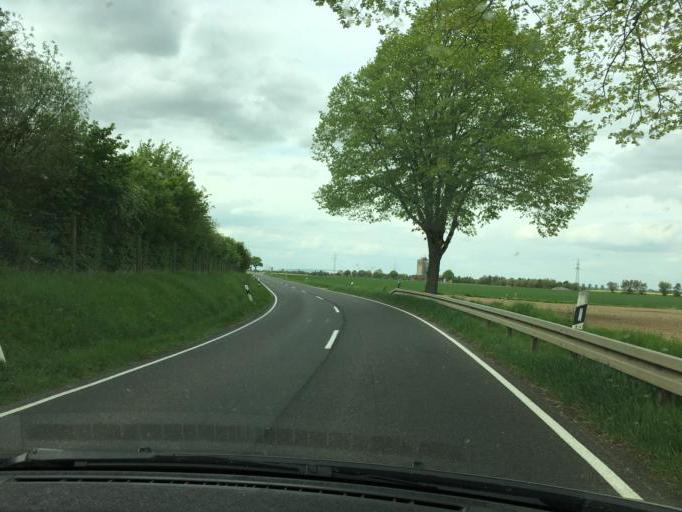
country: DE
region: North Rhine-Westphalia
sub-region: Regierungsbezirk Koln
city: Vettweiss
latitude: 50.7700
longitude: 6.5550
